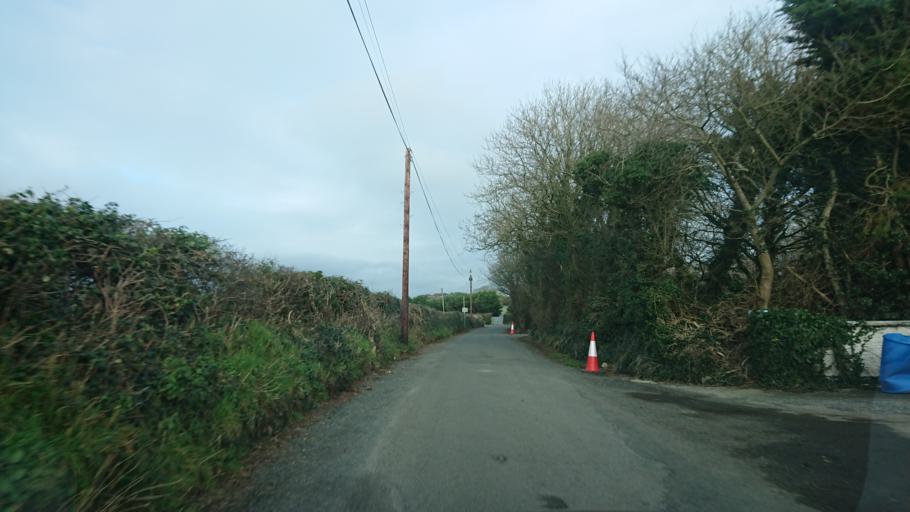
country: IE
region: Munster
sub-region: Waterford
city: Tra Mhor
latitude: 52.1581
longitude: -7.2145
